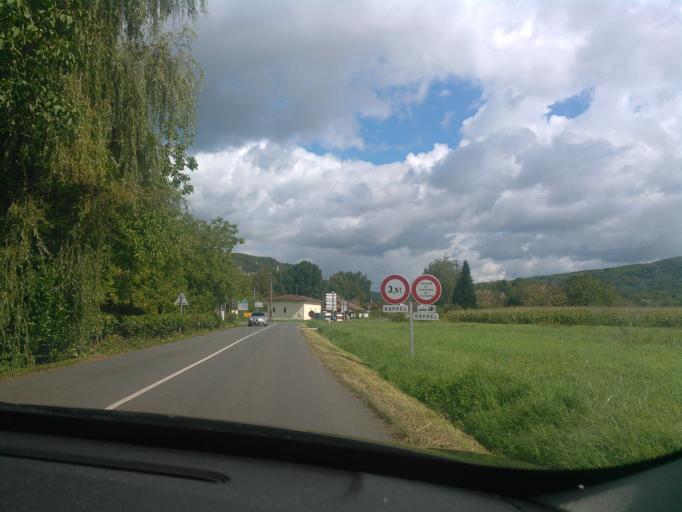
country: FR
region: Aquitaine
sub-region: Departement de la Dordogne
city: Cenac-et-Saint-Julien
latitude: 44.8327
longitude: 1.1532
